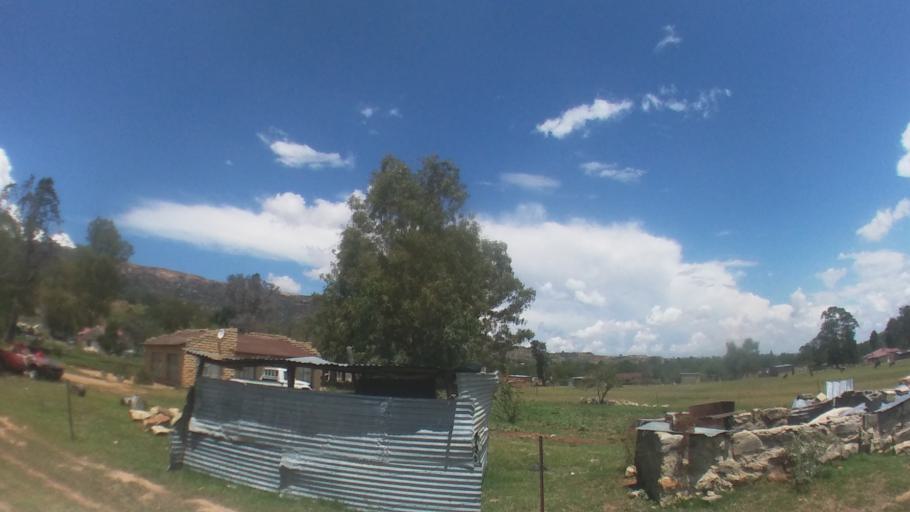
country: LS
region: Maseru
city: Nako
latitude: -29.6199
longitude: 27.5121
